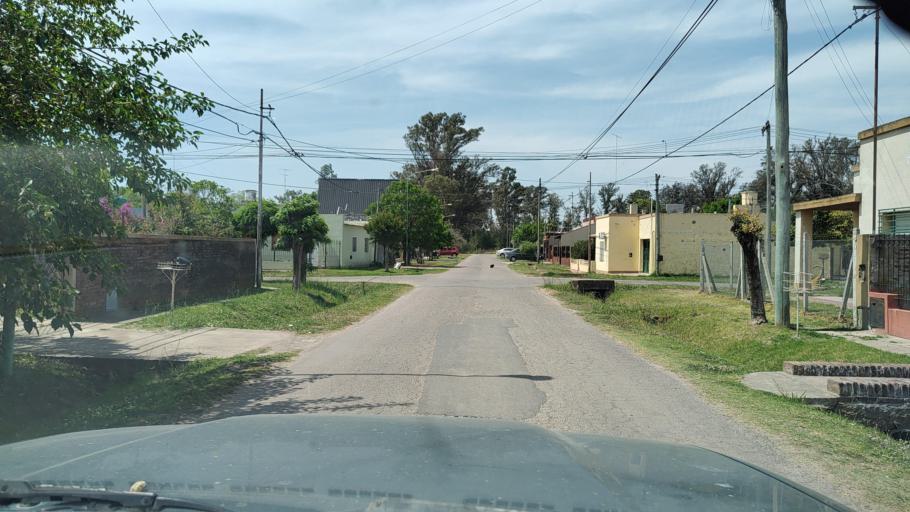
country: AR
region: Buenos Aires
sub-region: Partido de Lujan
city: Lujan
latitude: -34.6014
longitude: -59.1713
